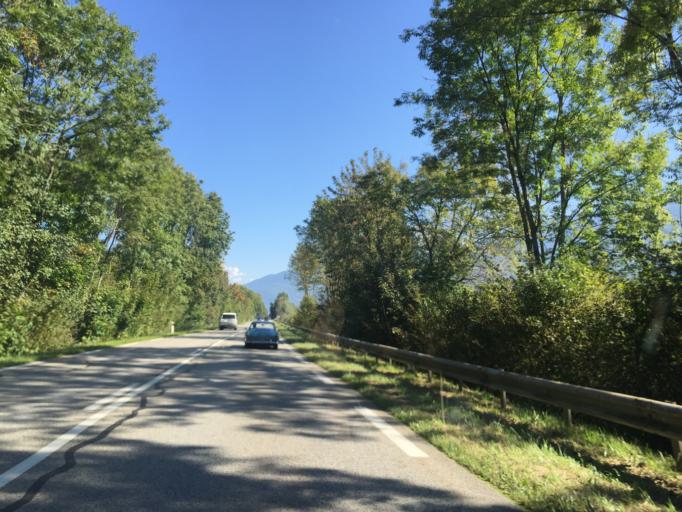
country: FR
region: Rhone-Alpes
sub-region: Departement de la Savoie
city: Gresy-sur-Isere
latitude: 45.6087
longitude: 6.2852
